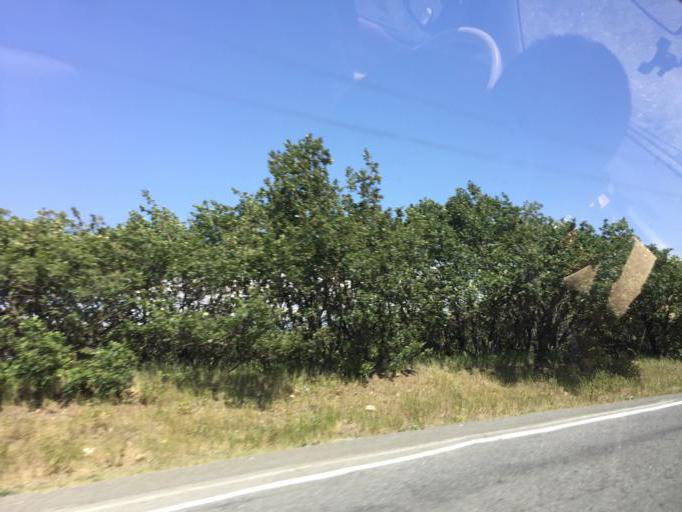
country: AM
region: Vayots' Dzori Marz
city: Jermuk
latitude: 39.7090
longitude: 45.6736
